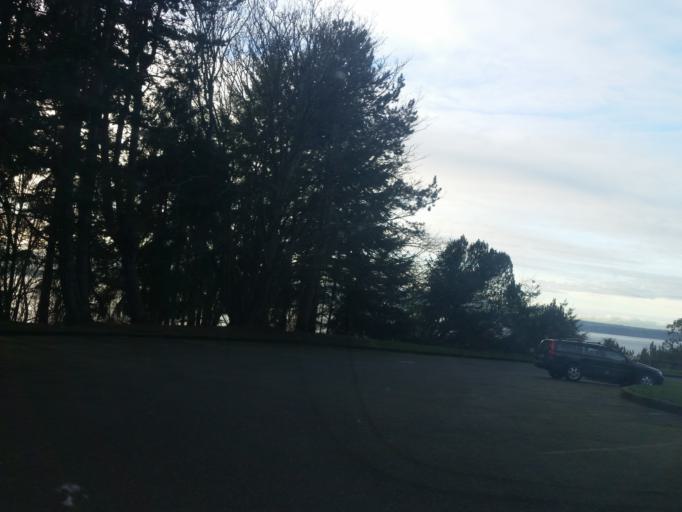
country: US
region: Washington
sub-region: King County
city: Shoreline
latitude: 47.7123
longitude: -122.3778
